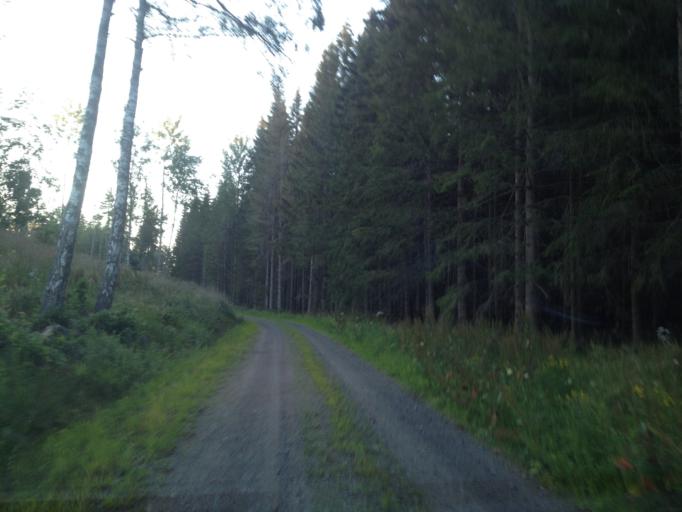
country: SE
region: Kalmar
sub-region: Vasterviks Kommun
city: Overum
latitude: 58.0151
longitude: 16.1194
